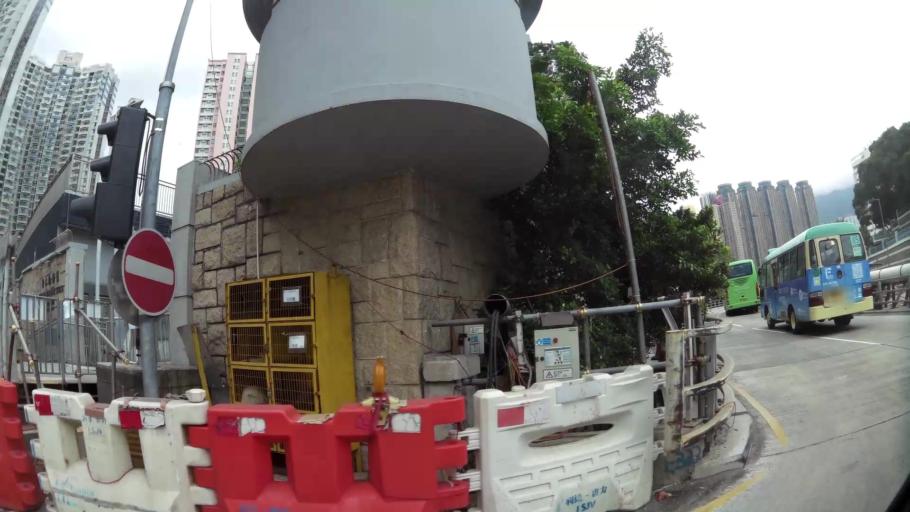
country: HK
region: Wong Tai Sin
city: Wong Tai Sin
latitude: 22.3388
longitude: 114.1963
